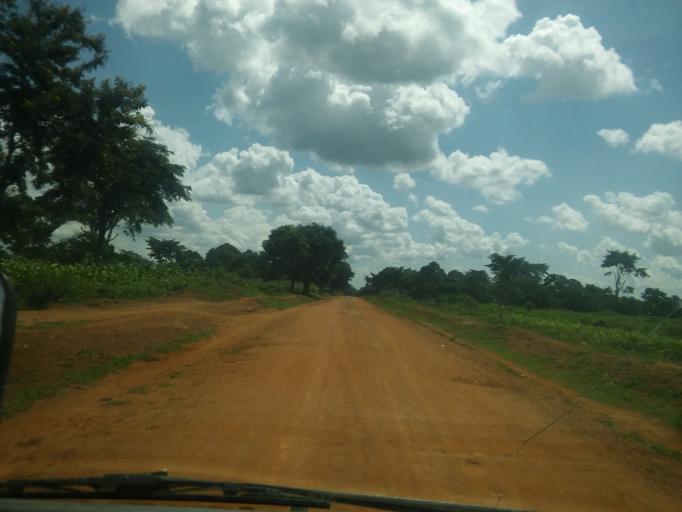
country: UG
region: Eastern Region
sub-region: Pallisa District
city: Pallisa
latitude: 1.1522
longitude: 33.8057
